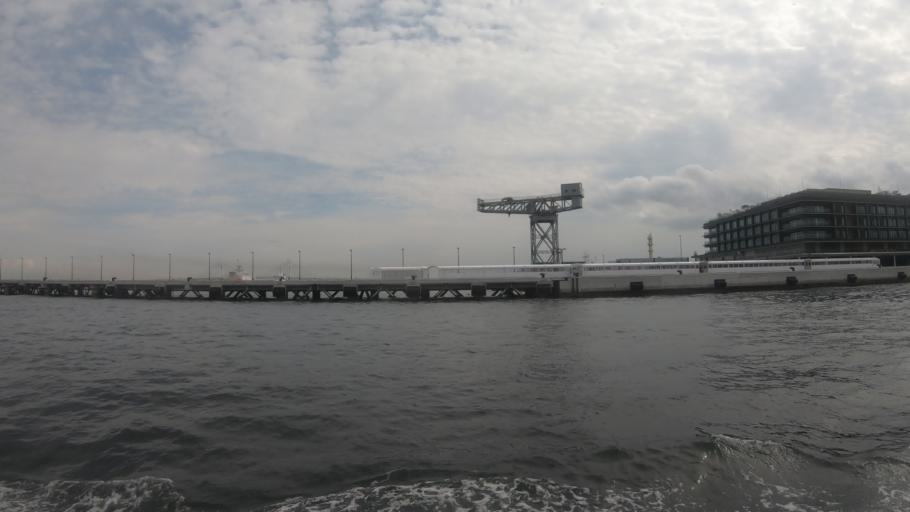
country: JP
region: Kanagawa
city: Yokohama
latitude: 35.4577
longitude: 139.6414
